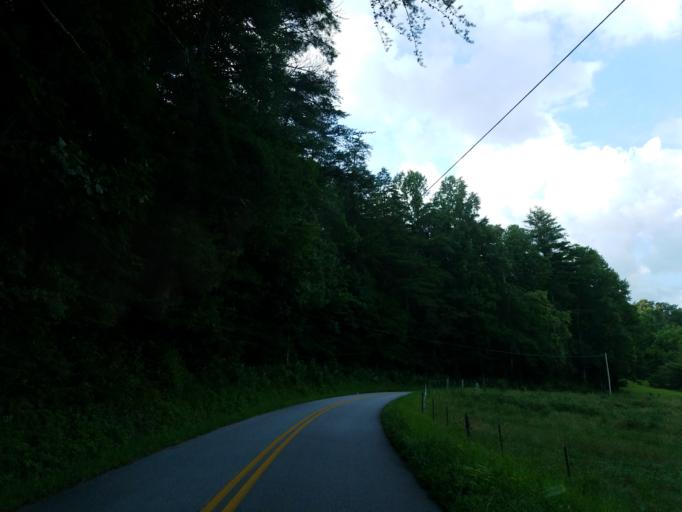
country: US
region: Georgia
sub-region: Lumpkin County
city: Dahlonega
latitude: 34.7084
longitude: -84.0768
